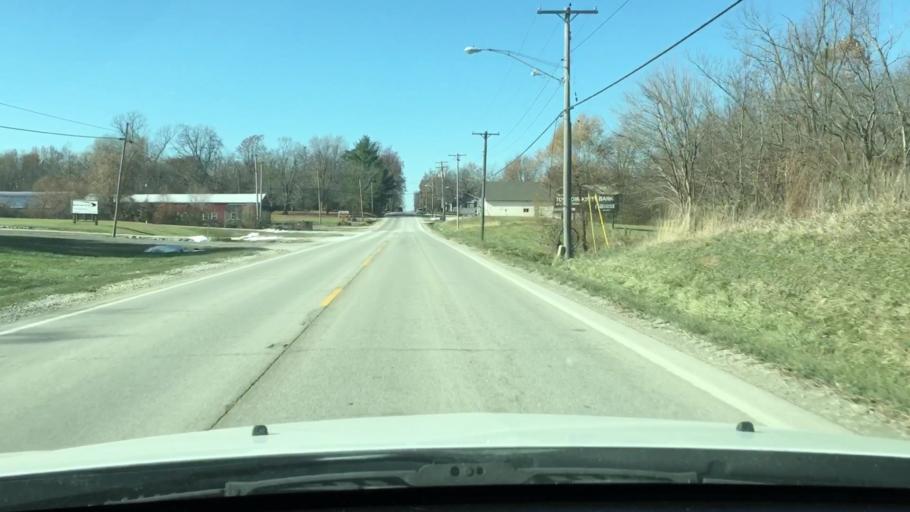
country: US
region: Illinois
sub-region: Pike County
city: Pittsfield
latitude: 39.6068
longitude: -90.7883
